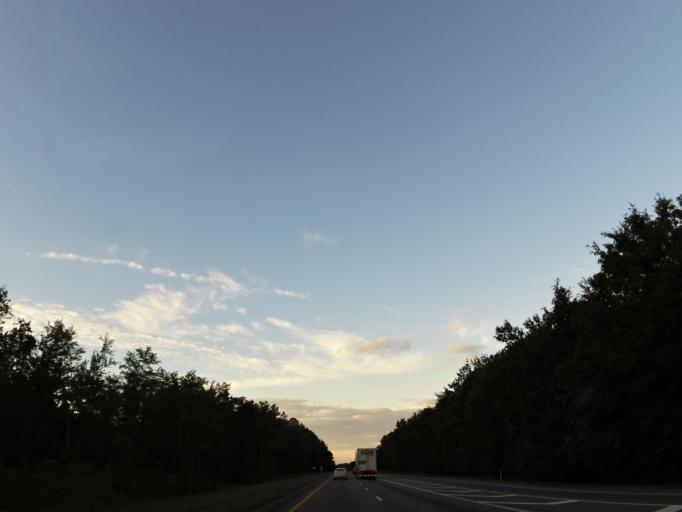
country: US
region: Tennessee
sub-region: McMinn County
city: Athens
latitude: 35.4295
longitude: -84.6862
